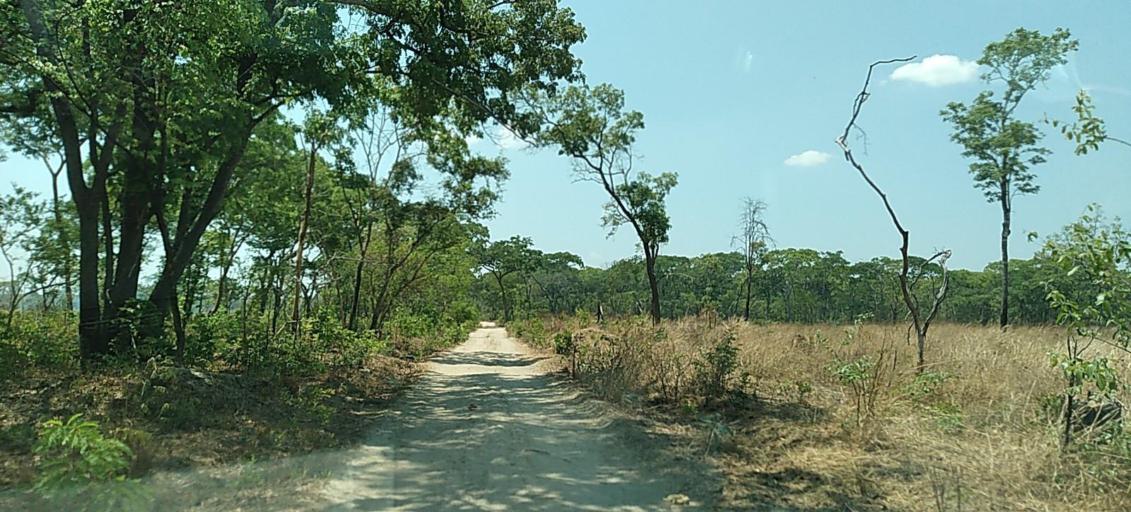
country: ZM
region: Copperbelt
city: Mpongwe
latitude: -13.6391
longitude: 28.4824
